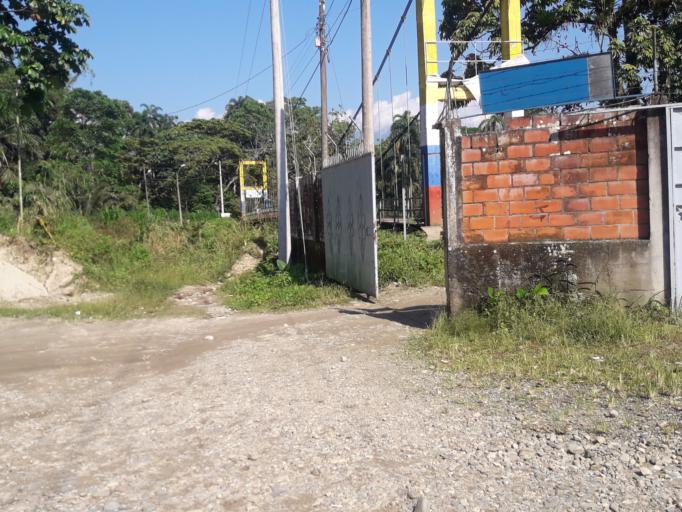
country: EC
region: Napo
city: Tena
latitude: -0.9927
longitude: -77.8184
